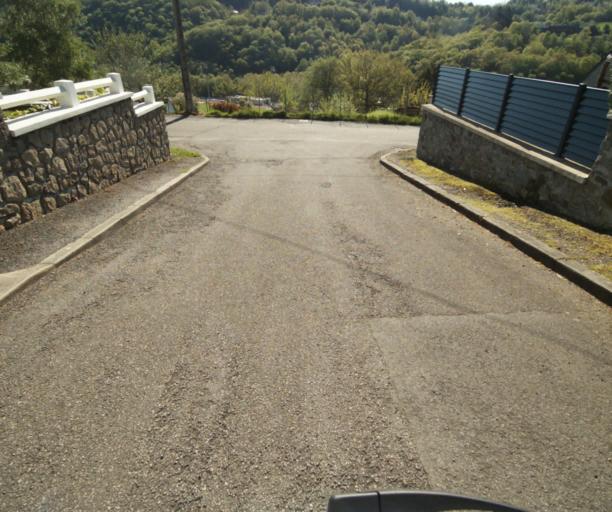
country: FR
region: Limousin
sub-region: Departement de la Correze
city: Tulle
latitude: 45.2782
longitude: 1.7792
